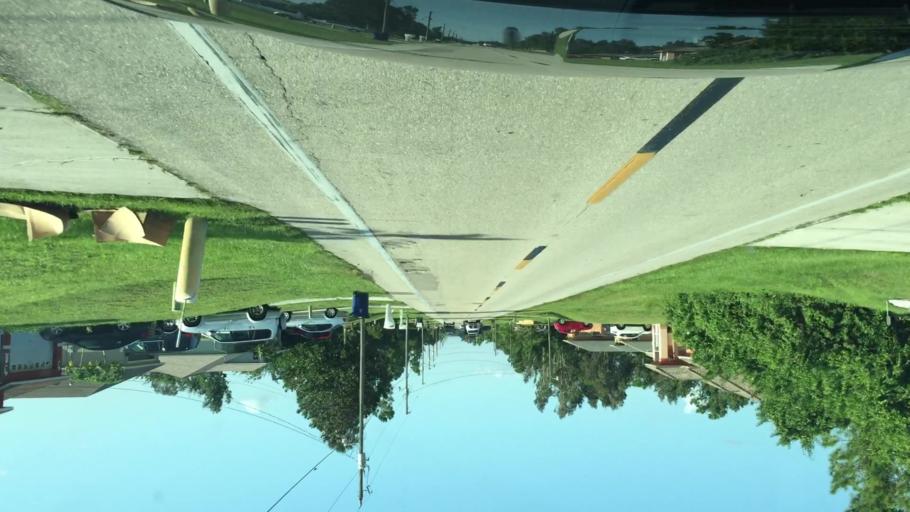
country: US
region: Florida
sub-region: Lee County
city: Buckingham
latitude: 26.6313
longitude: -81.7505
